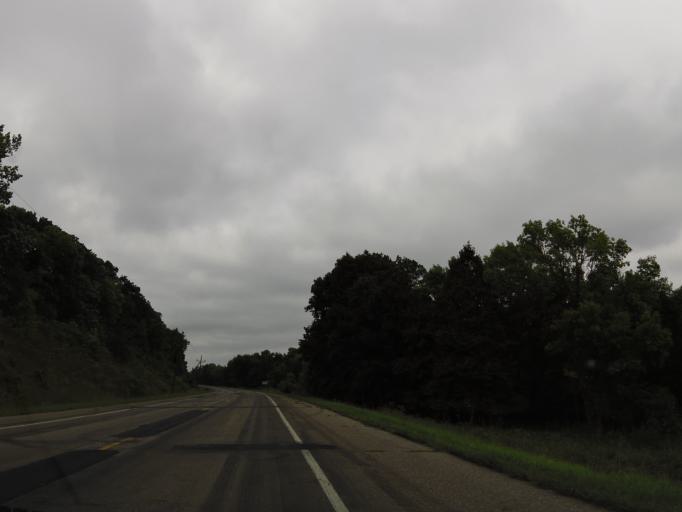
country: US
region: Minnesota
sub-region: Yellow Medicine County
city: Granite Falls
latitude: 44.8622
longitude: -95.6326
